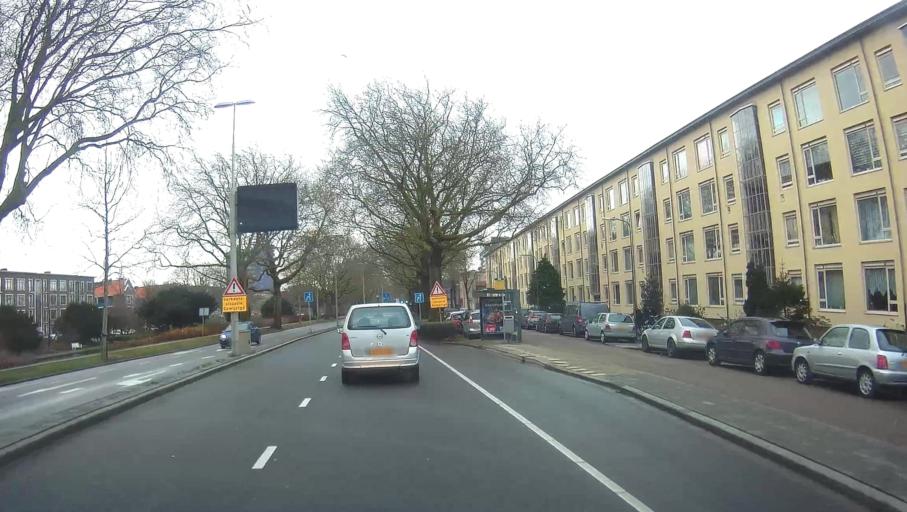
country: NL
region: South Holland
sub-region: Gemeente Den Haag
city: The Hague
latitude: 52.0540
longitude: 4.2963
